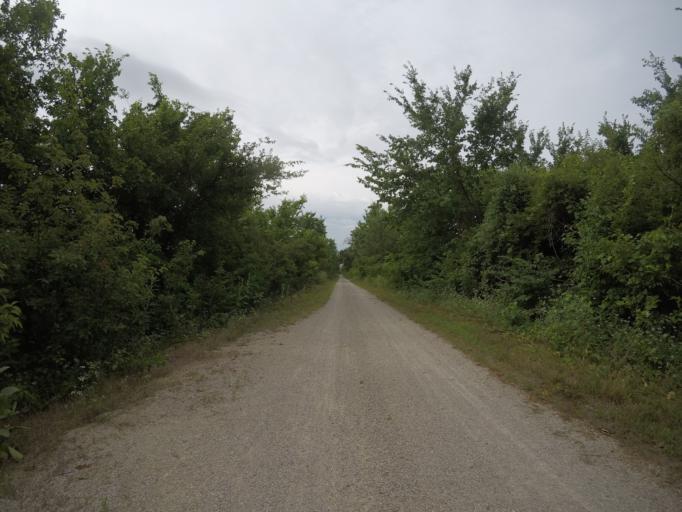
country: US
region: Kansas
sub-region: Franklin County
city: Ottawa
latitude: 38.5258
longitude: -95.2722
